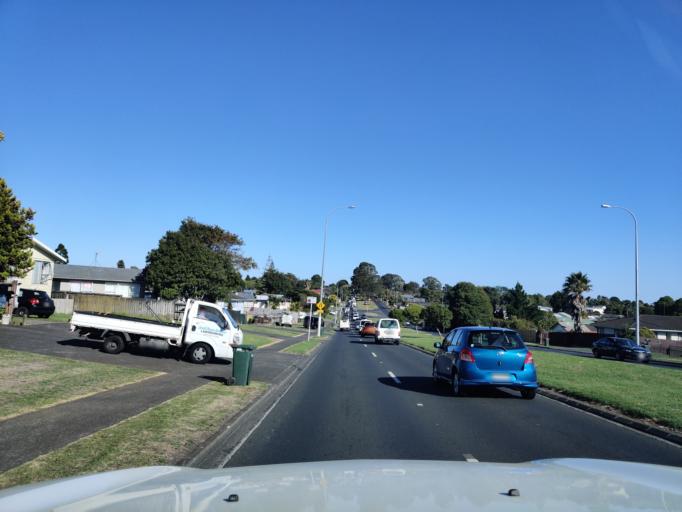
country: NZ
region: Auckland
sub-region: Auckland
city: Wiri
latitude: -37.0196
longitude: 174.8626
